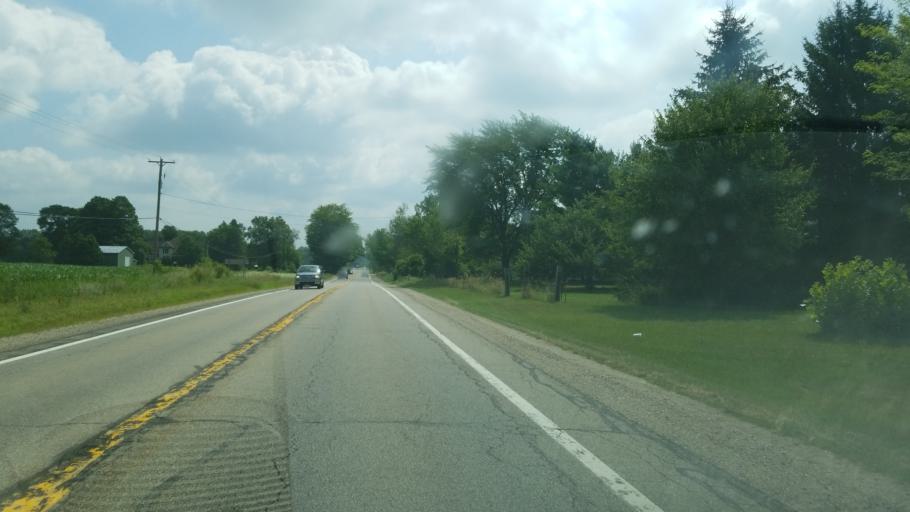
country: US
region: Michigan
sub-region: Kent County
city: Kent City
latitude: 43.2197
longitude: -85.7003
